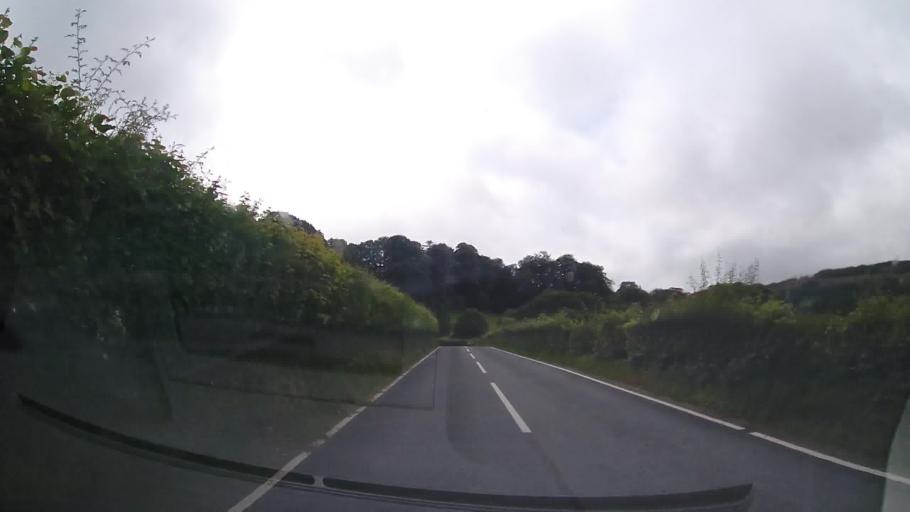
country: GB
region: Wales
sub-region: Denbighshire
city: Llandrillo
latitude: 52.9166
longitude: -3.5052
